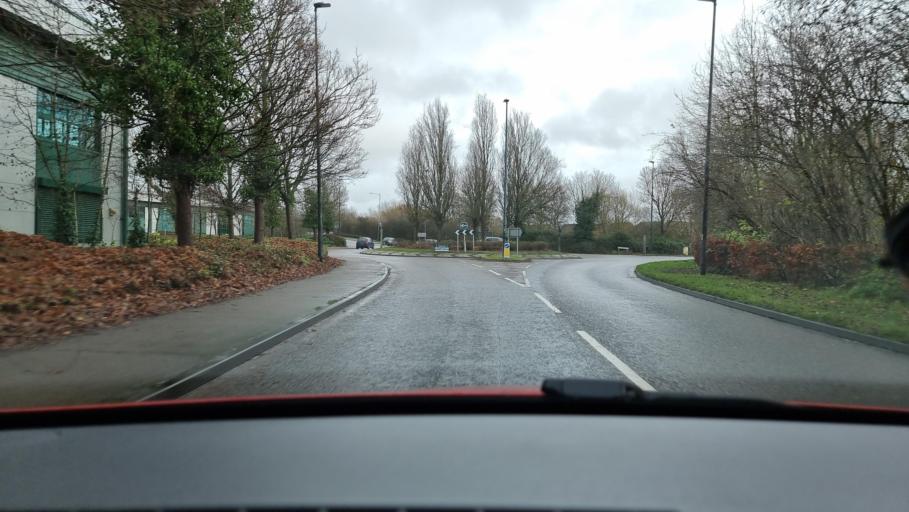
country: GB
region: England
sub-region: Buckinghamshire
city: Aylesbury
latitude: 51.8187
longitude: -0.8367
